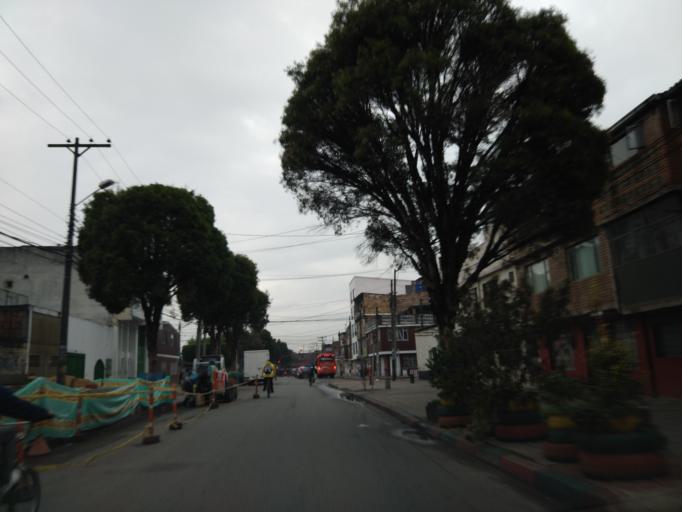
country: CO
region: Cundinamarca
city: Funza
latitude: 4.6823
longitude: -74.1369
